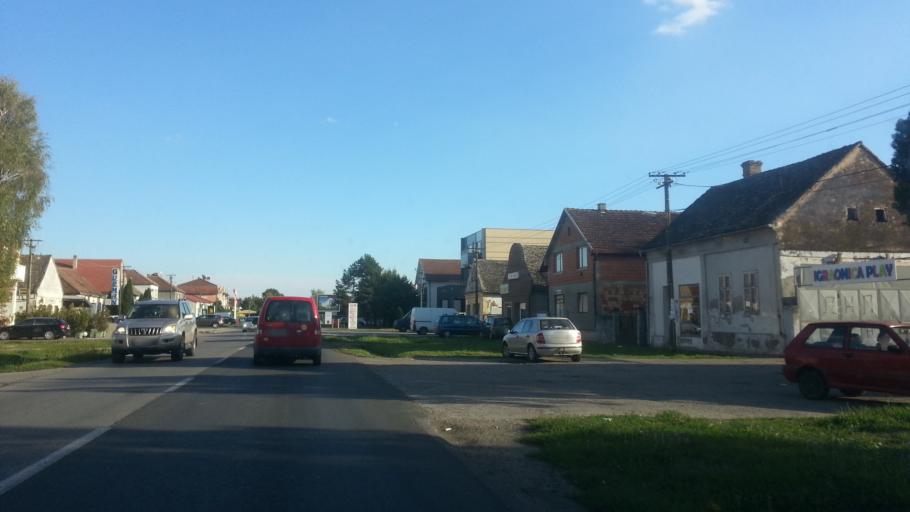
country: RS
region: Autonomna Pokrajina Vojvodina
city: Nova Pazova
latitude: 44.9434
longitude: 20.2206
